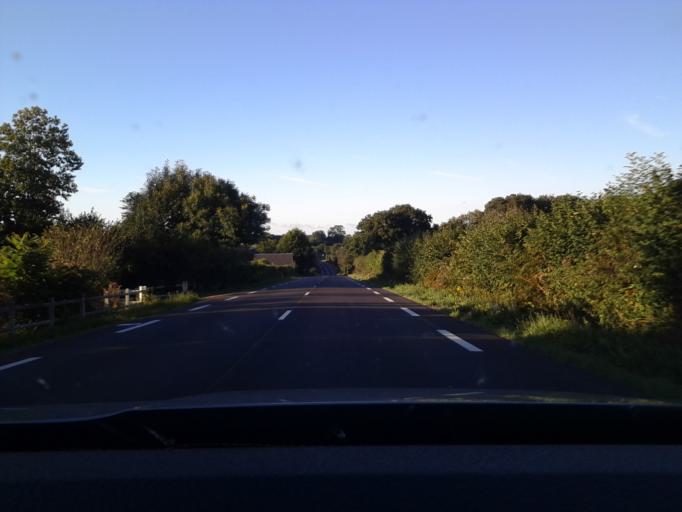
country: FR
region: Lower Normandy
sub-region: Departement de la Manche
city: La Haye-du-Puits
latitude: 49.3284
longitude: -1.5345
